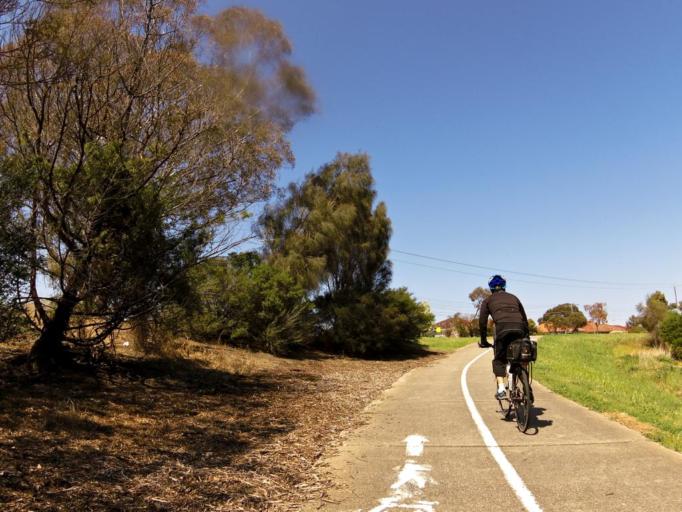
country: AU
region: Victoria
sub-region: Brimbank
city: Deer Park
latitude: -37.7749
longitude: 144.7963
